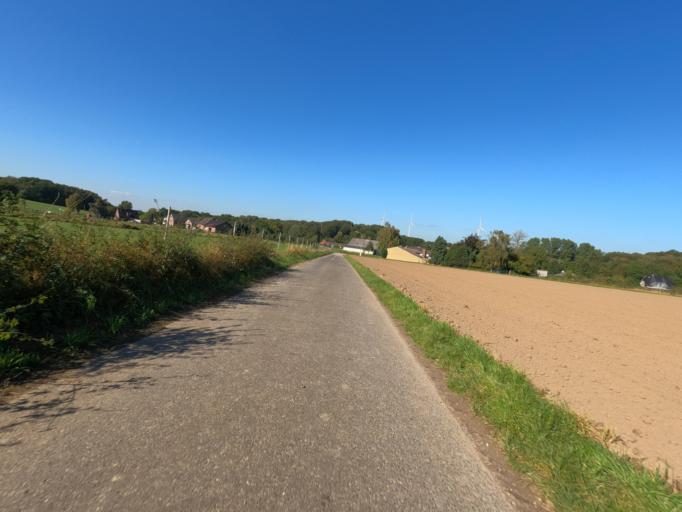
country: DE
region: North Rhine-Westphalia
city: Huckelhoven
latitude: 51.0477
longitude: 6.2611
